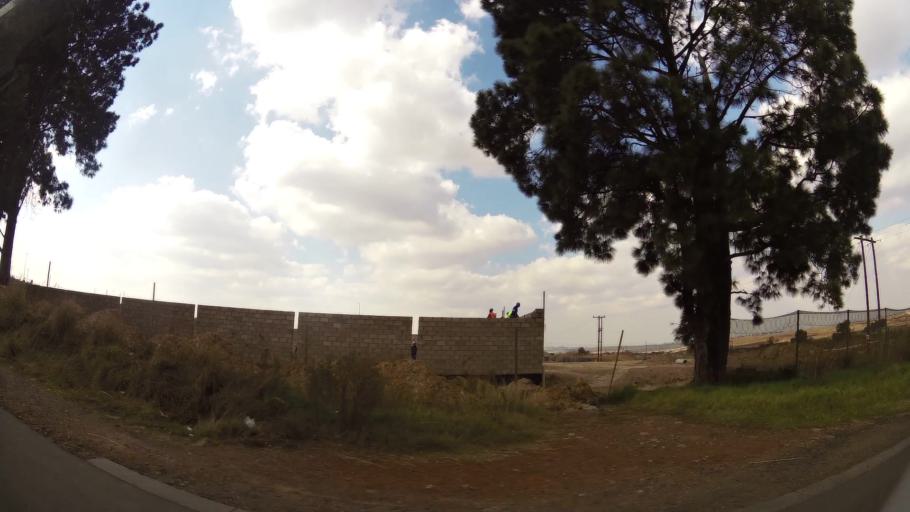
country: ZA
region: Mpumalanga
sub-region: Nkangala District Municipality
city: Delmas
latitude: -26.1044
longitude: 28.6783
